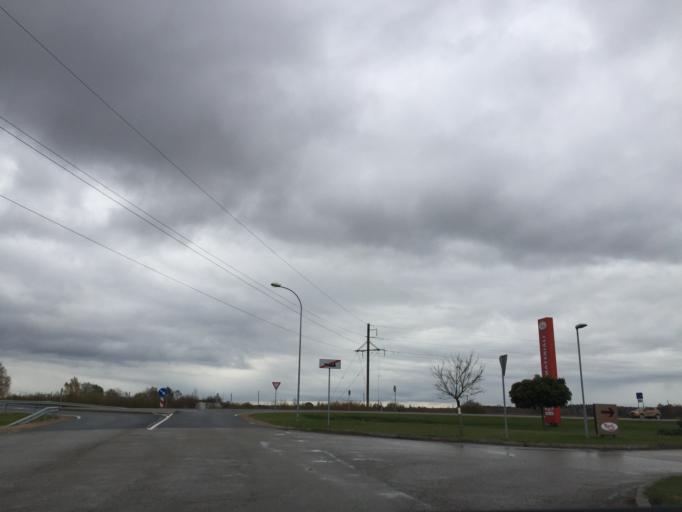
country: LV
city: Tireli
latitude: 56.9315
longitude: 23.5900
